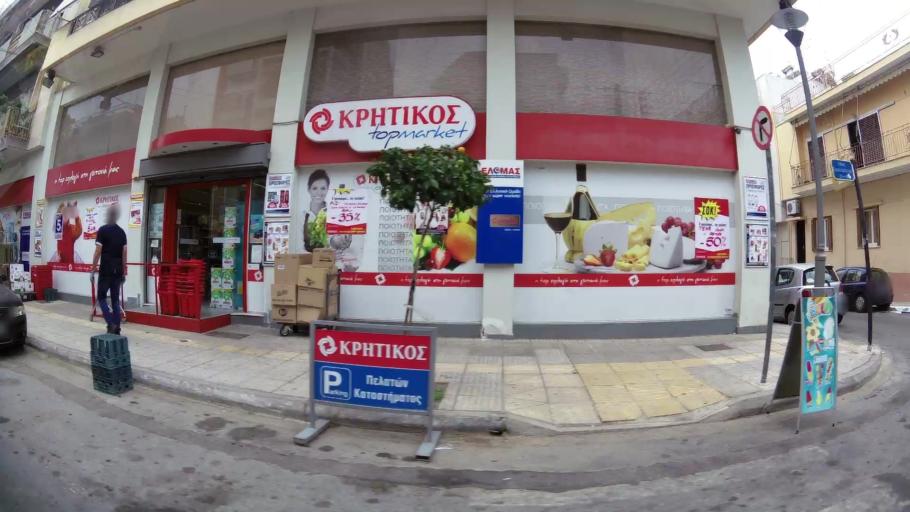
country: GR
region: Attica
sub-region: Nomarchia Athinas
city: Aigaleo
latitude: 37.9884
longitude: 23.6812
